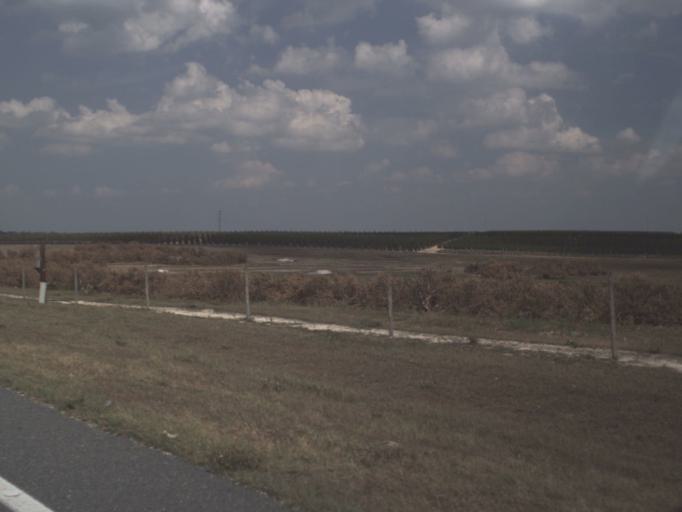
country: US
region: Florida
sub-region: Lake County
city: Groveland
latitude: 28.5917
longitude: -81.8476
